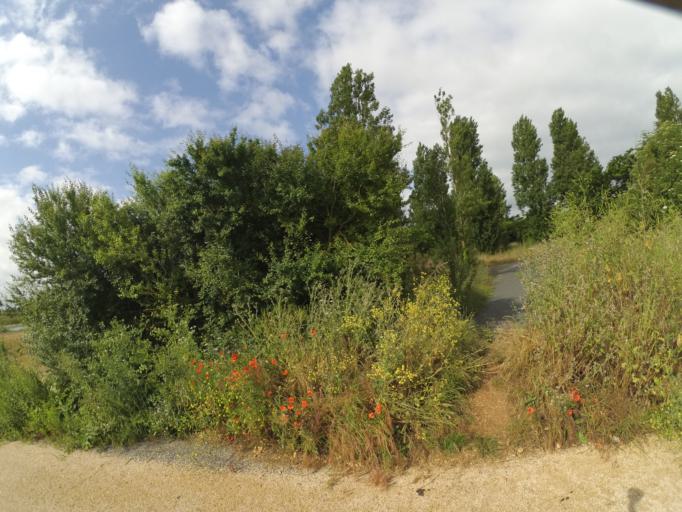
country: FR
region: Poitou-Charentes
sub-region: Departement de la Charente-Maritime
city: Angoulins
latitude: 46.1125
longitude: -1.1221
